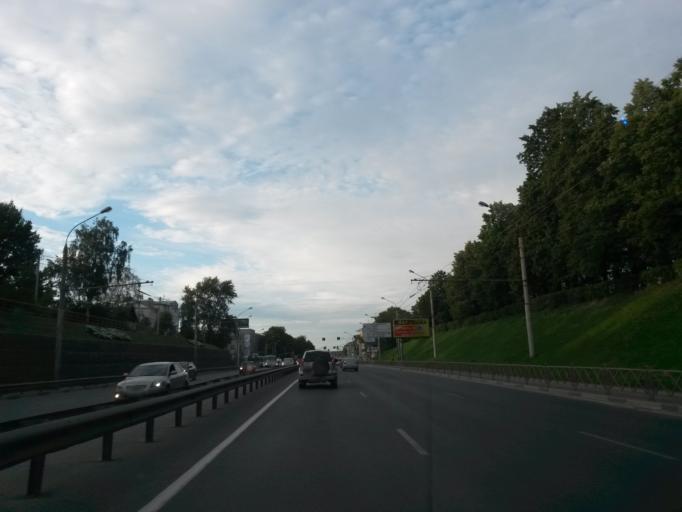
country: RU
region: Jaroslavl
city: Yaroslavl
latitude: 57.6032
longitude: 39.8776
